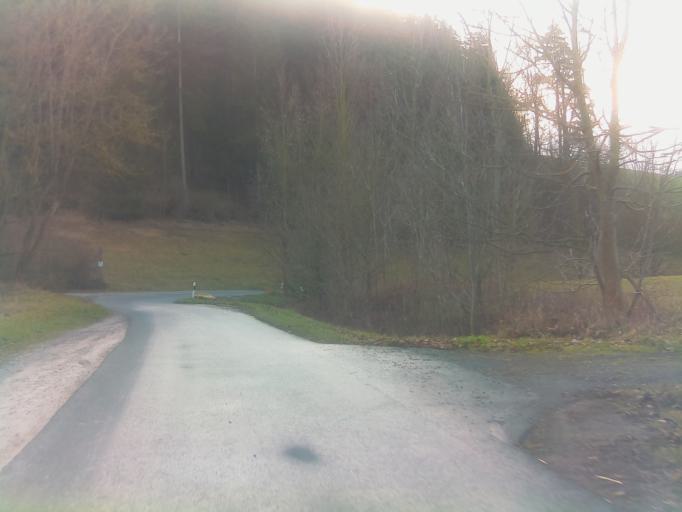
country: DE
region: Thuringia
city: Rottenbach
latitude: 50.7242
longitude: 11.1994
